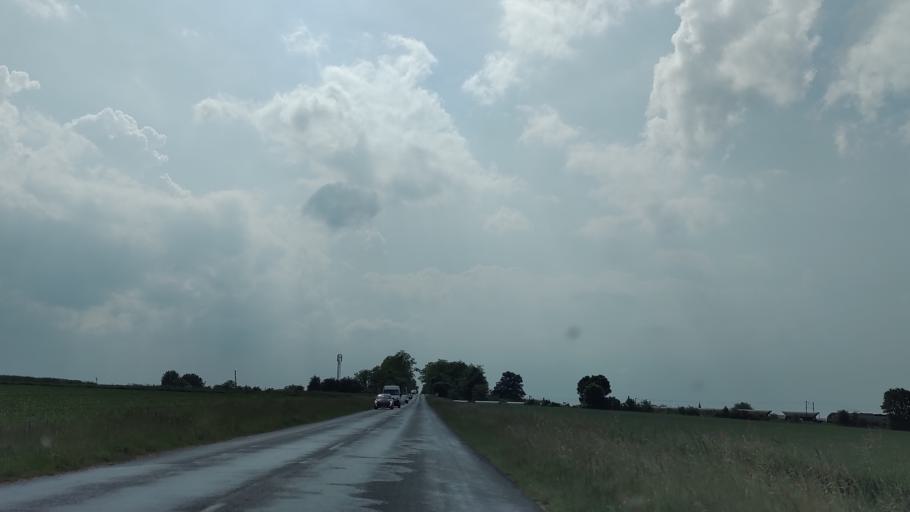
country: FR
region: Ile-de-France
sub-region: Departement de Seine-et-Marne
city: Juilly
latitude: 49.0092
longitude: 2.6857
